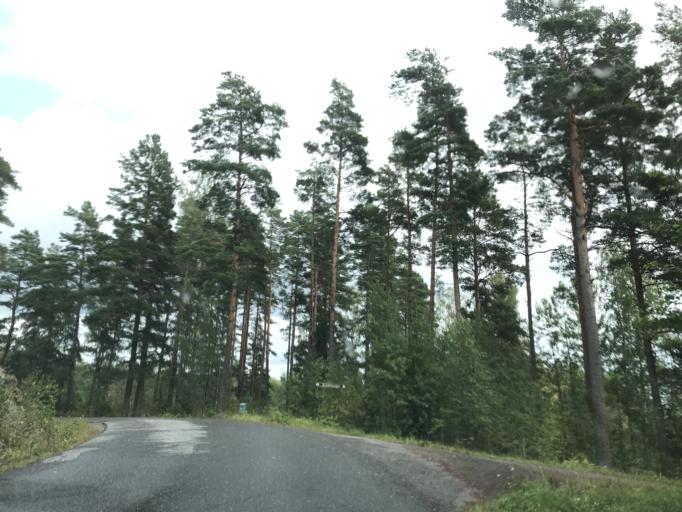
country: FI
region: Varsinais-Suomi
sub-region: Salo
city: Pernioe
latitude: 60.0731
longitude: 23.1139
